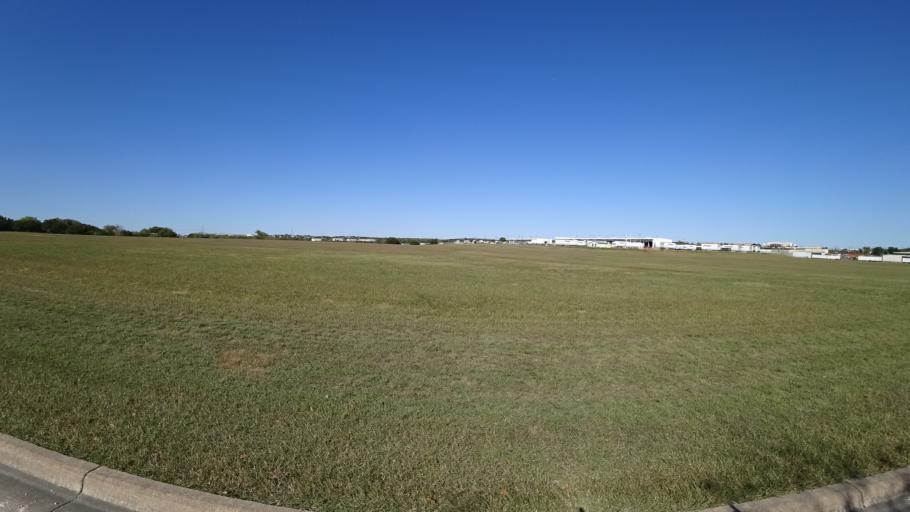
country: US
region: Texas
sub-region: Travis County
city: Hornsby Bend
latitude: 30.2879
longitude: -97.6368
